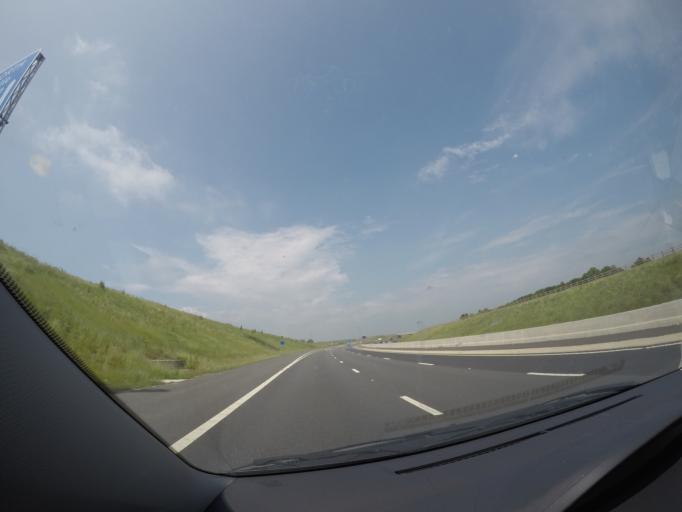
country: GB
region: England
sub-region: North Yorkshire
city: Catterick
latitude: 54.3753
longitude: -1.6458
